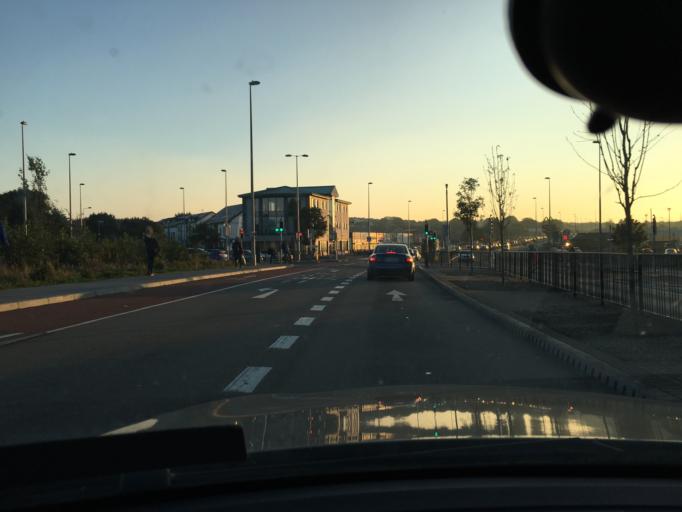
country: IE
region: Connaught
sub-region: County Galway
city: Gaillimh
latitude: 53.2764
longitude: -9.0738
